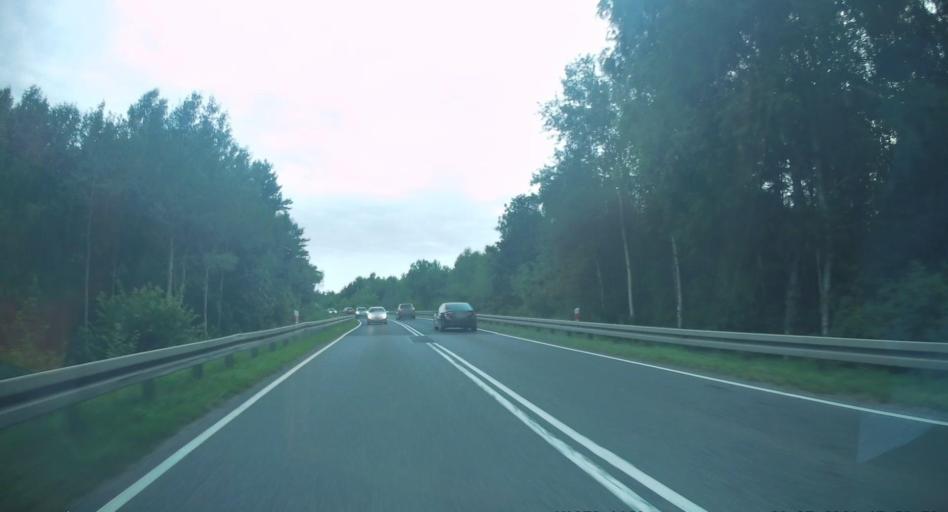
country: PL
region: Lodz Voivodeship
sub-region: Powiat radomszczanski
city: Kamiensk
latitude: 51.1866
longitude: 19.4955
